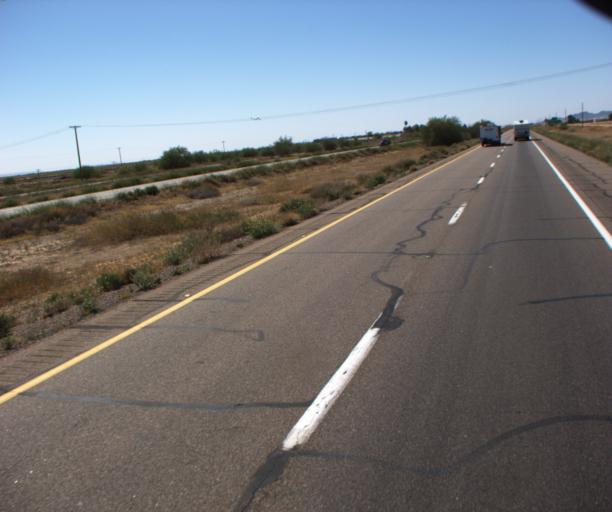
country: US
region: Arizona
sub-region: Maricopa County
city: Gila Bend
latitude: 32.9241
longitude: -112.8719
